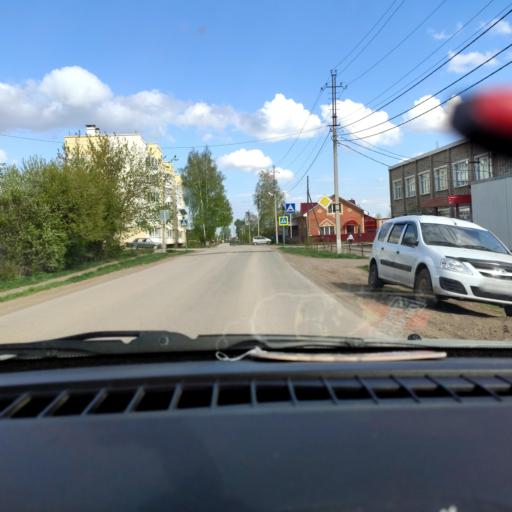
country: RU
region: Perm
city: Kudymkar
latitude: 59.0072
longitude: 54.6634
